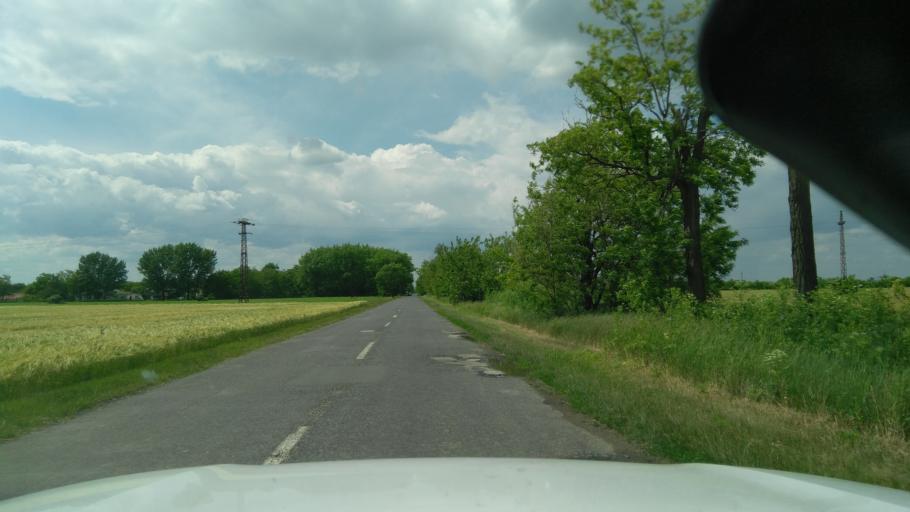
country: HU
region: Bekes
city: Magyarbanhegyes
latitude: 46.4672
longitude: 20.9479
